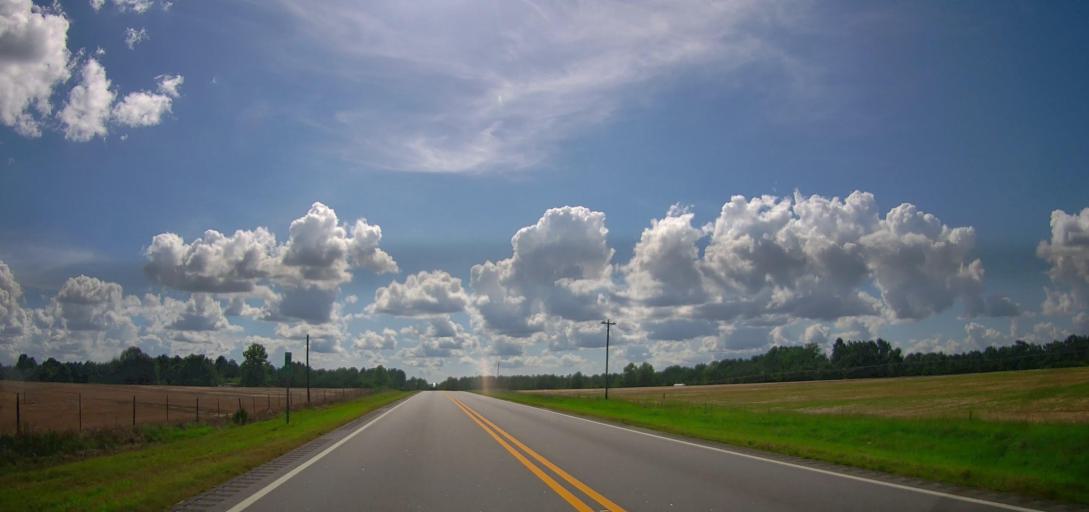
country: US
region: Alabama
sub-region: Lee County
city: Auburn
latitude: 32.4353
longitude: -85.4063
